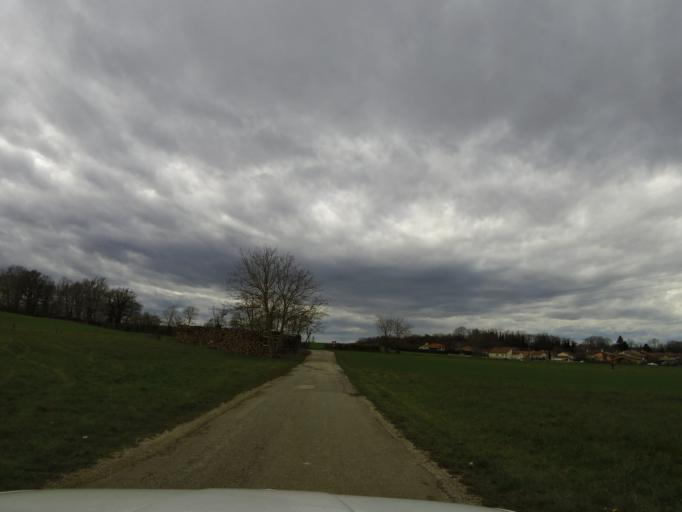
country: FR
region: Rhone-Alpes
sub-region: Departement de l'Ain
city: Leyment
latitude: 45.9171
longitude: 5.3013
